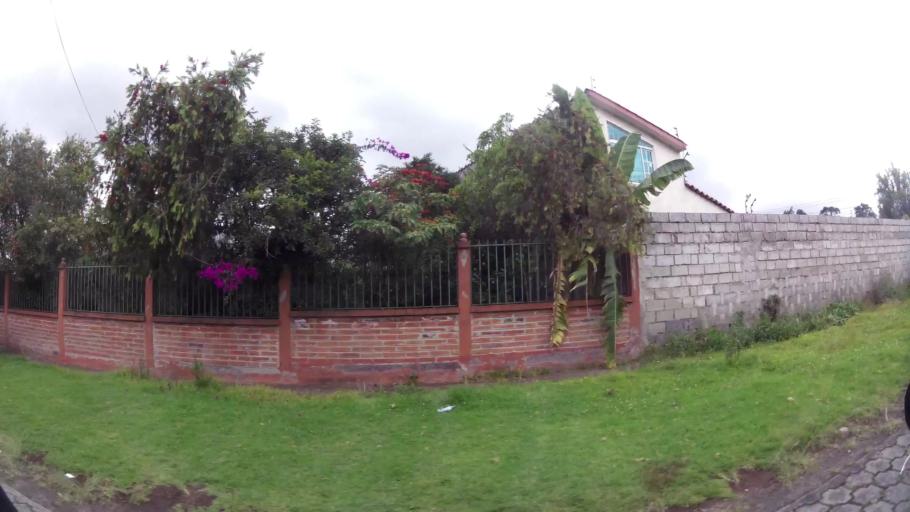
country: EC
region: Pichincha
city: Sangolqui
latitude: -0.3207
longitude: -78.4674
